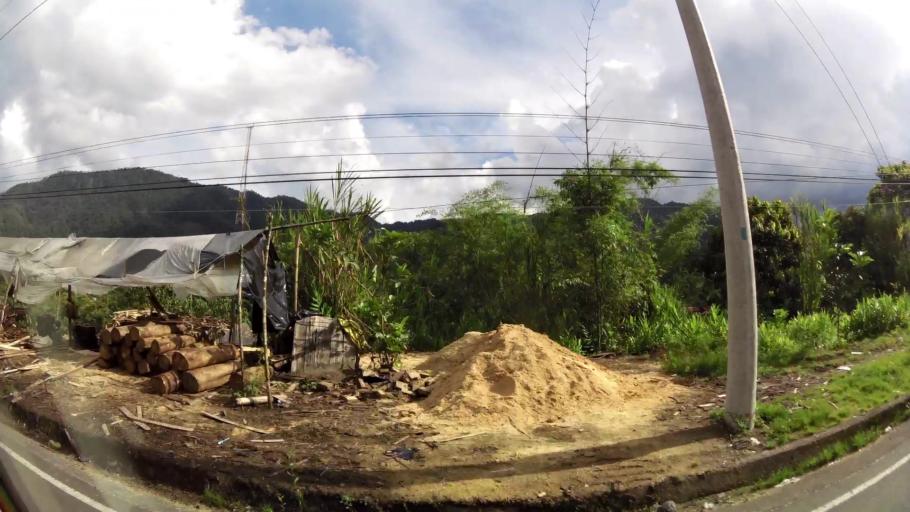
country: EC
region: Tungurahua
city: Banos
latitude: -1.4127
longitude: -78.2074
